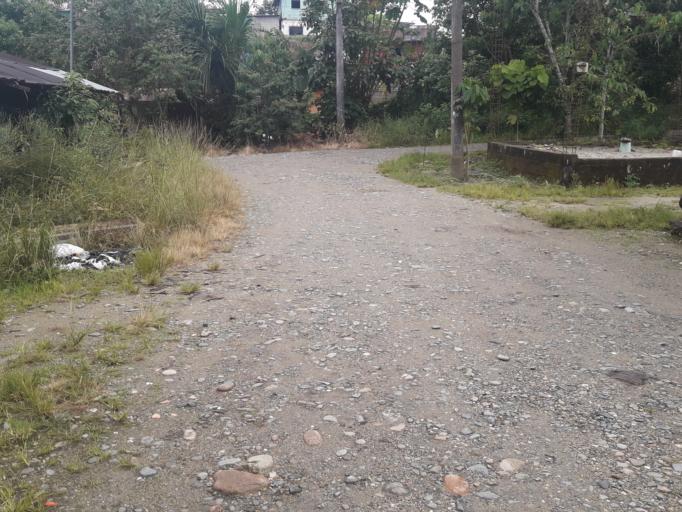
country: EC
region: Napo
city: Tena
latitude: -0.9877
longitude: -77.8248
